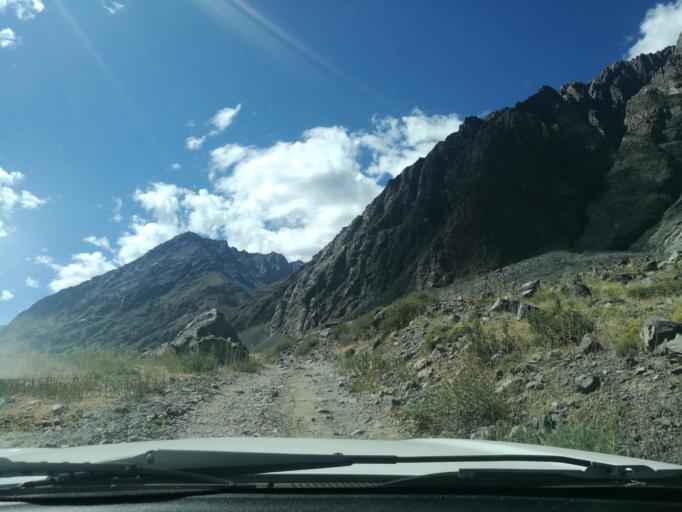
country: CL
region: O'Higgins
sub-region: Provincia de Cachapoal
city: Machali
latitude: -34.4060
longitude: -70.2456
